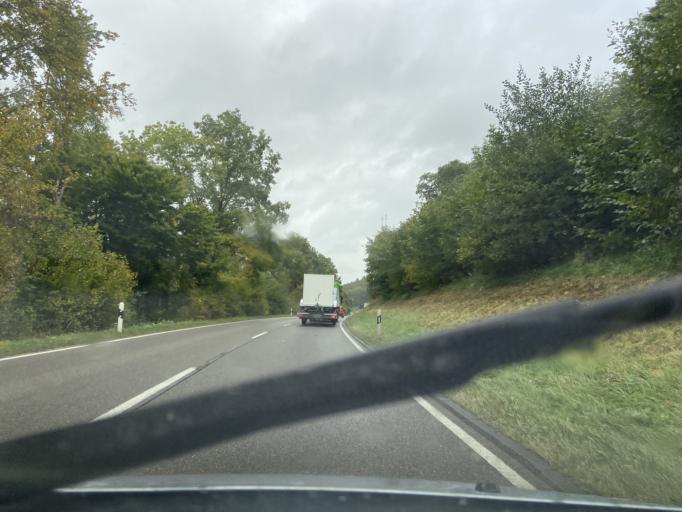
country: DE
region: Baden-Wuerttemberg
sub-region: Tuebingen Region
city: Krauchenwies
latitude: 48.0081
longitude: 9.2019
